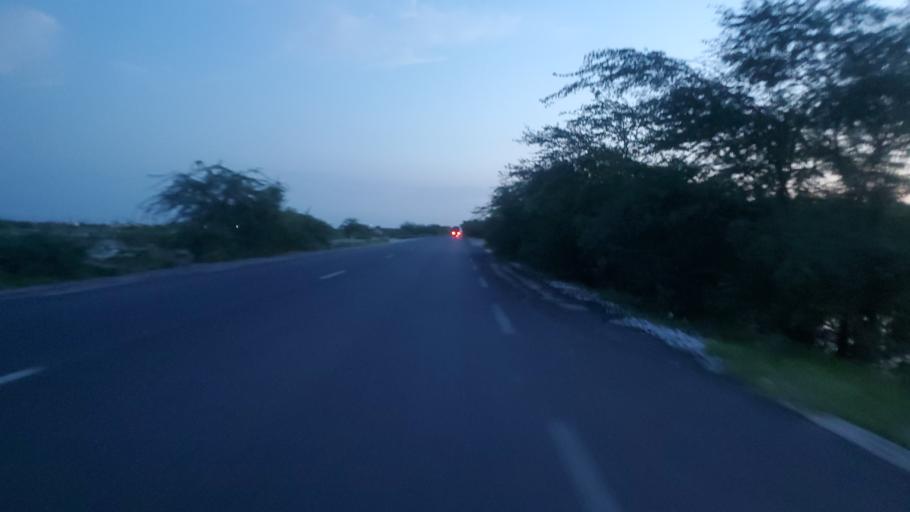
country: SN
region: Saint-Louis
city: Saint-Louis
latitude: 16.0652
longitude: -16.3934
